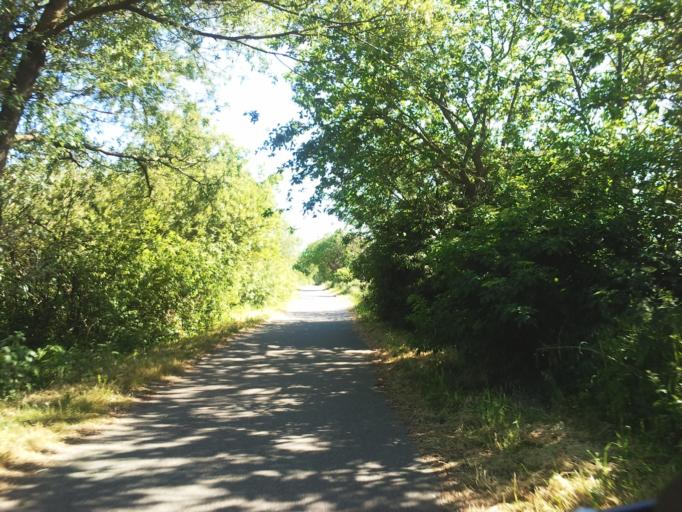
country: DE
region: Mecklenburg-Vorpommern
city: Nienhagen
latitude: 54.1459
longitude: 12.1892
